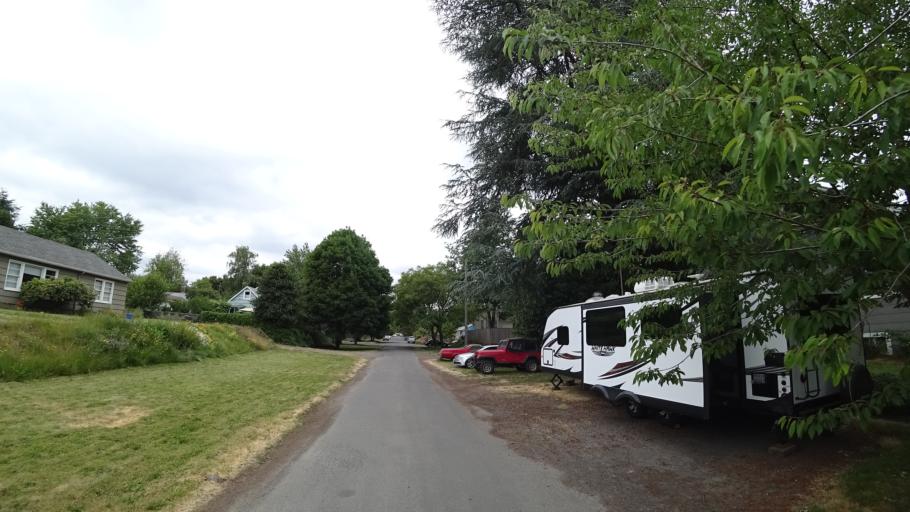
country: US
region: Oregon
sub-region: Multnomah County
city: Lents
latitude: 45.5146
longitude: -122.5833
